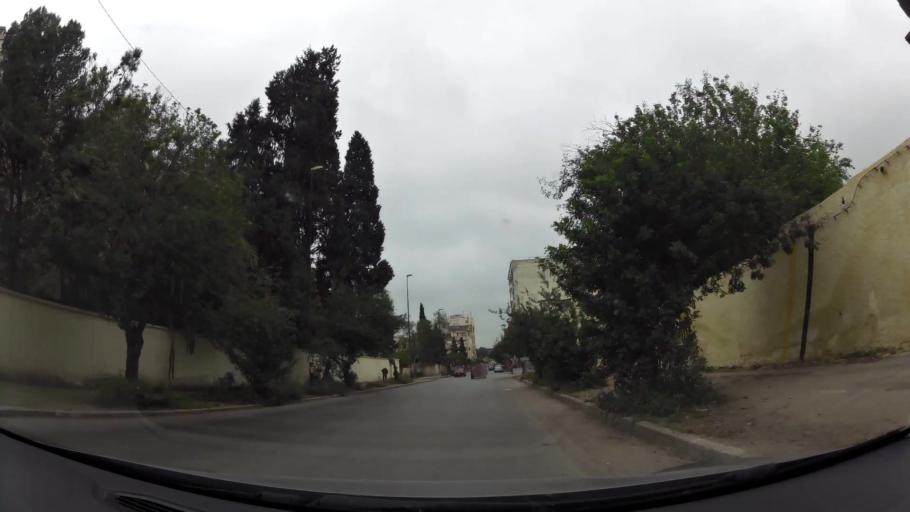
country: MA
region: Fes-Boulemane
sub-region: Fes
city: Fes
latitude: 34.0450
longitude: -5.0005
